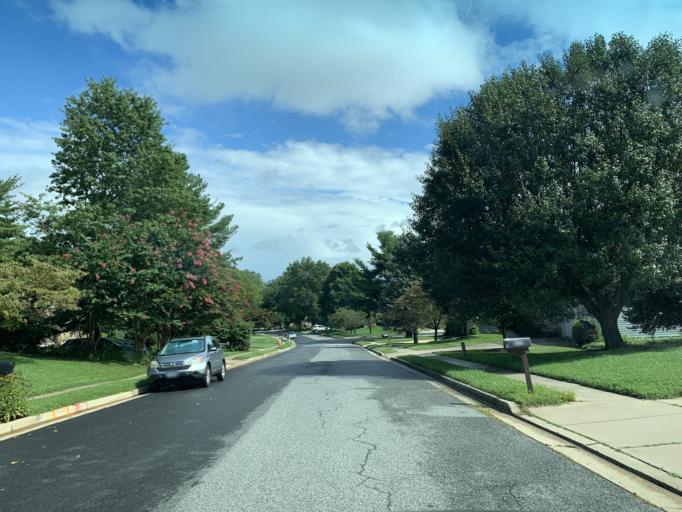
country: US
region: Maryland
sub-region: Baltimore County
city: Timonium
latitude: 39.4485
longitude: -76.6100
